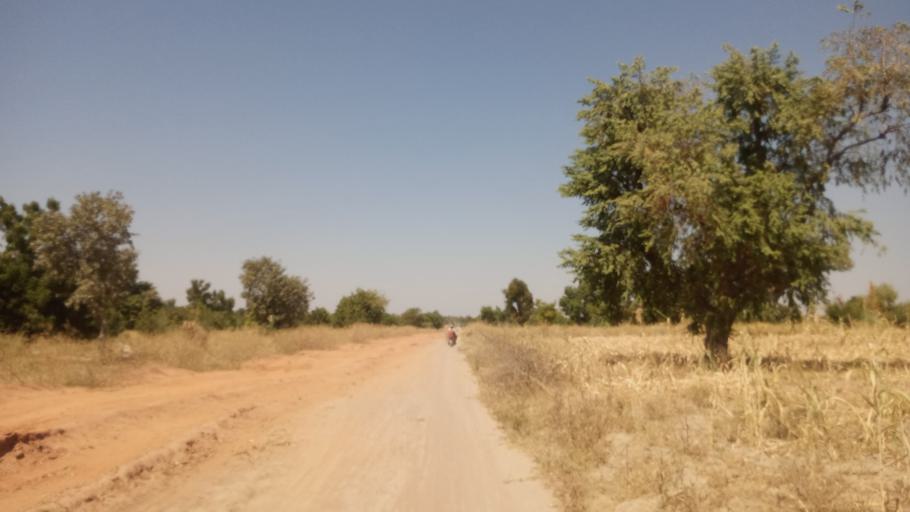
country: NG
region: Adamawa
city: Mayo Belwa
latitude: 9.0876
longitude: 12.0267
